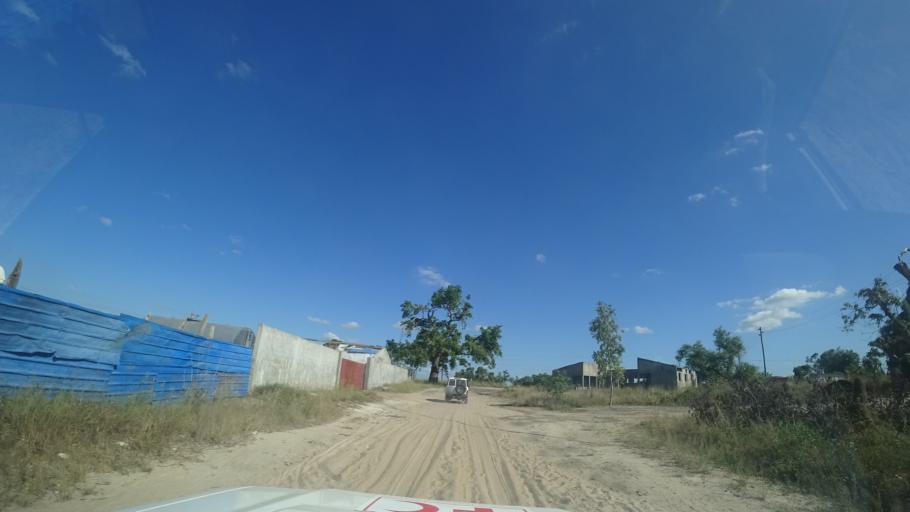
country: MZ
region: Sofala
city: Dondo
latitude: -19.5078
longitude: 34.6097
